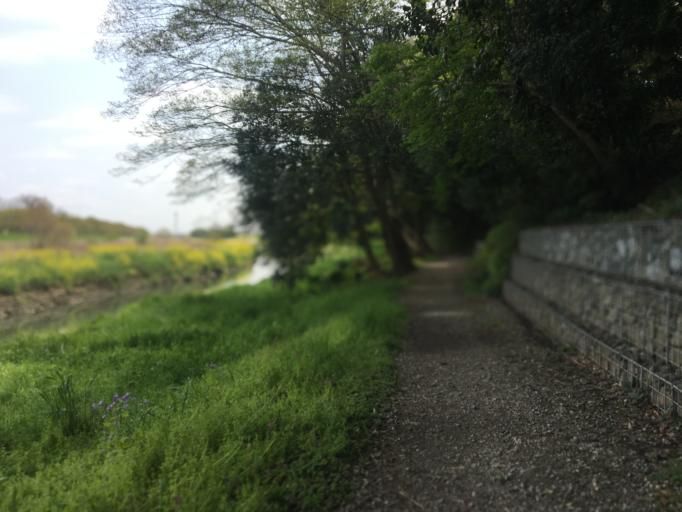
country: JP
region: Saitama
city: Kamifukuoka
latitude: 35.8820
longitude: 139.5263
